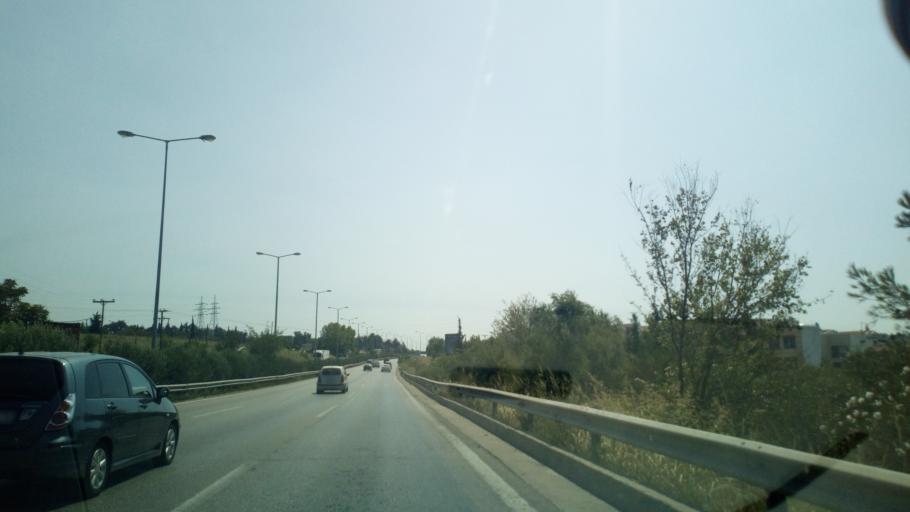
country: GR
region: Central Macedonia
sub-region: Nomos Thessalonikis
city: Pylaia
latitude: 40.6045
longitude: 22.9990
